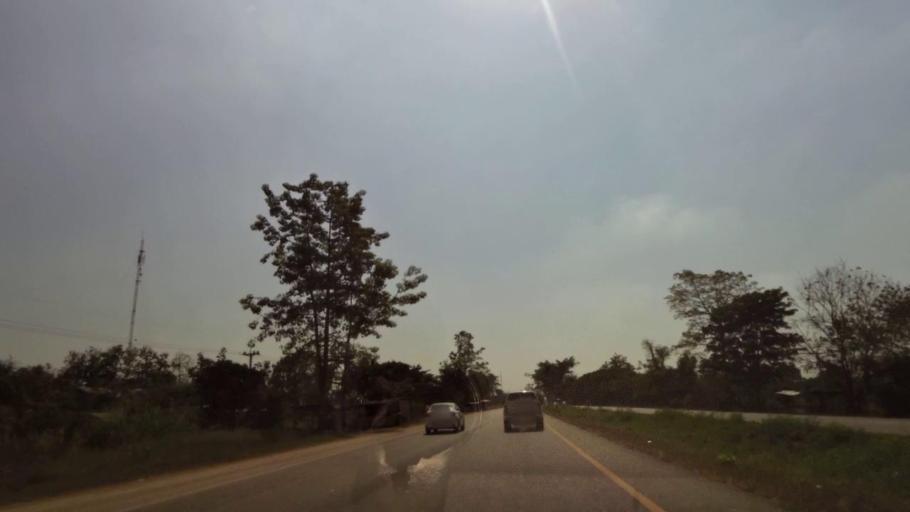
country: TH
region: Phichit
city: Wachira Barami
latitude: 16.4209
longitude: 100.1440
